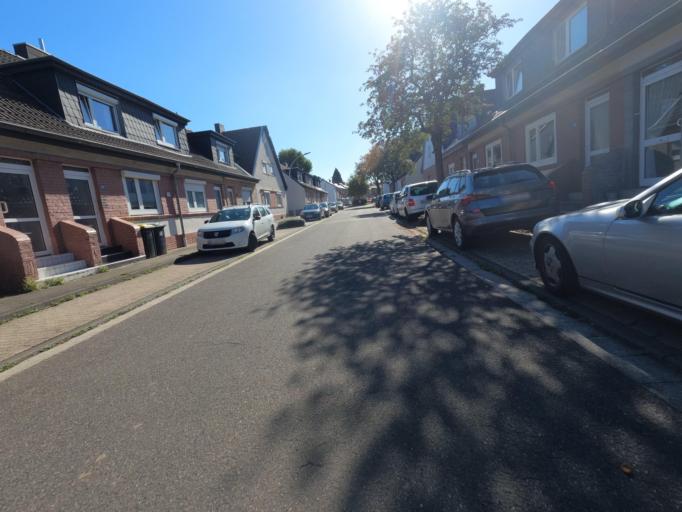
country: DE
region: North Rhine-Westphalia
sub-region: Regierungsbezirk Koln
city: Ubach-Palenberg
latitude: 50.9106
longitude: 6.1440
